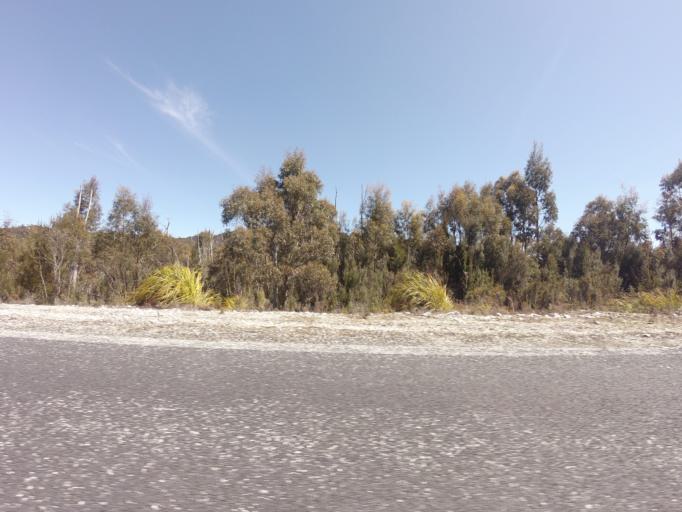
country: AU
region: Tasmania
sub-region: West Coast
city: Queenstown
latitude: -42.8004
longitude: 146.0917
